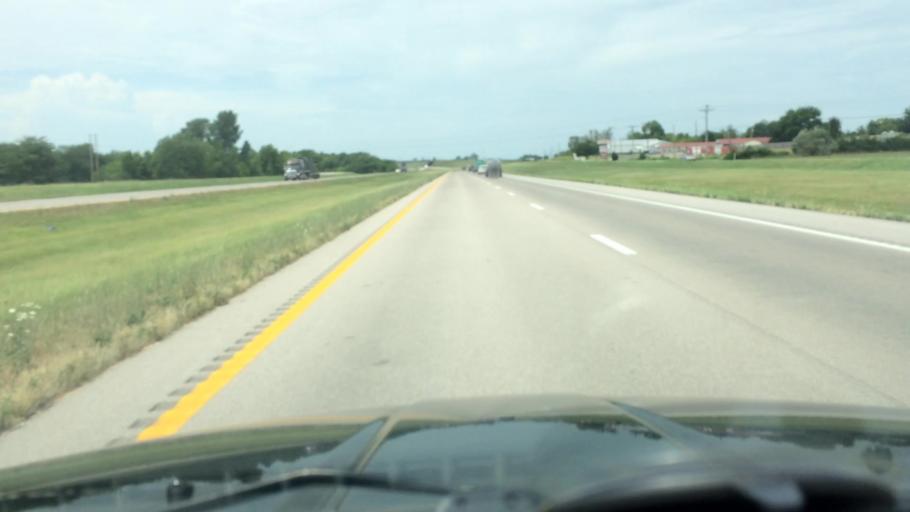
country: US
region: Missouri
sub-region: Polk County
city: Bolivar
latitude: 37.5664
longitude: -93.3944
